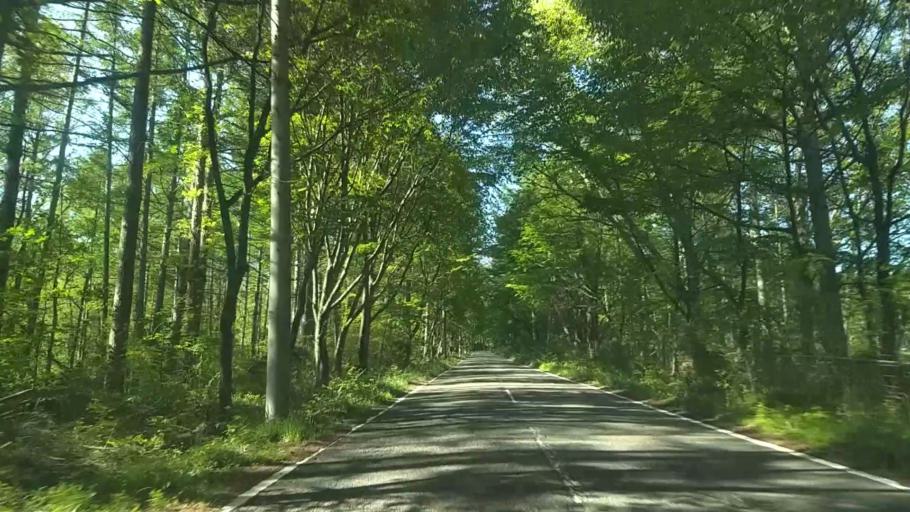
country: JP
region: Nagano
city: Chino
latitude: 35.8968
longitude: 138.3504
